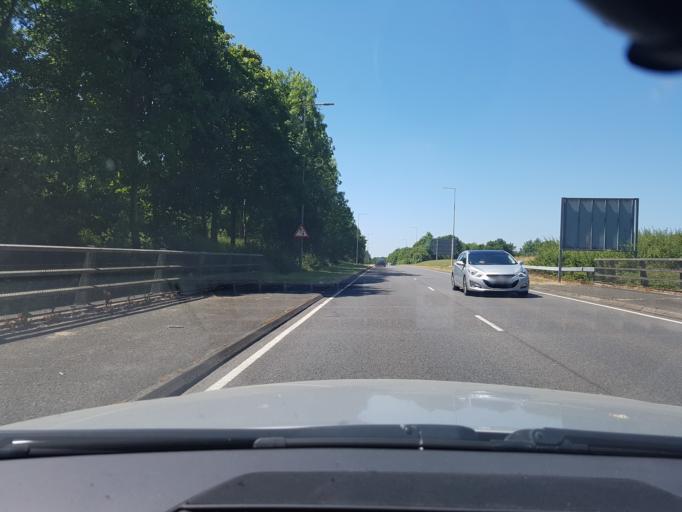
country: GB
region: England
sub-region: Milton Keynes
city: Milton Keynes
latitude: 52.0496
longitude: -0.7681
